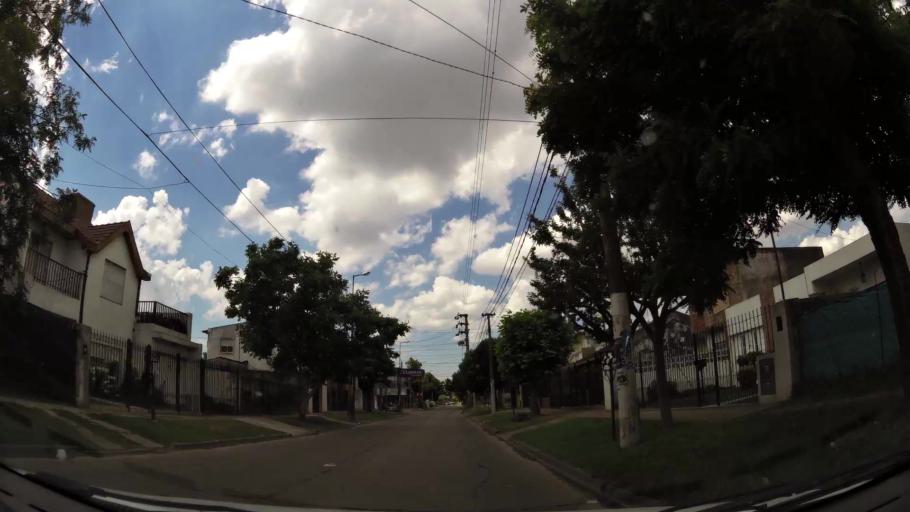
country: AR
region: Buenos Aires
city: Ituzaingo
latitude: -34.6415
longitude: -58.6749
